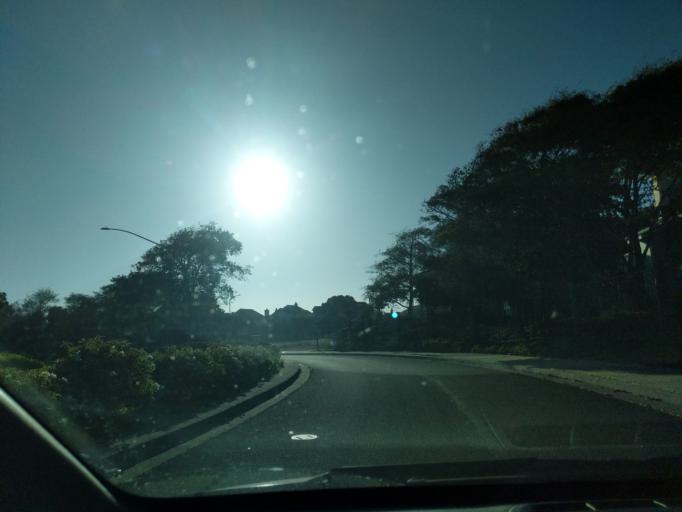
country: US
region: California
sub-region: Contra Costa County
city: Richmond
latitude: 37.9092
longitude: -122.3442
